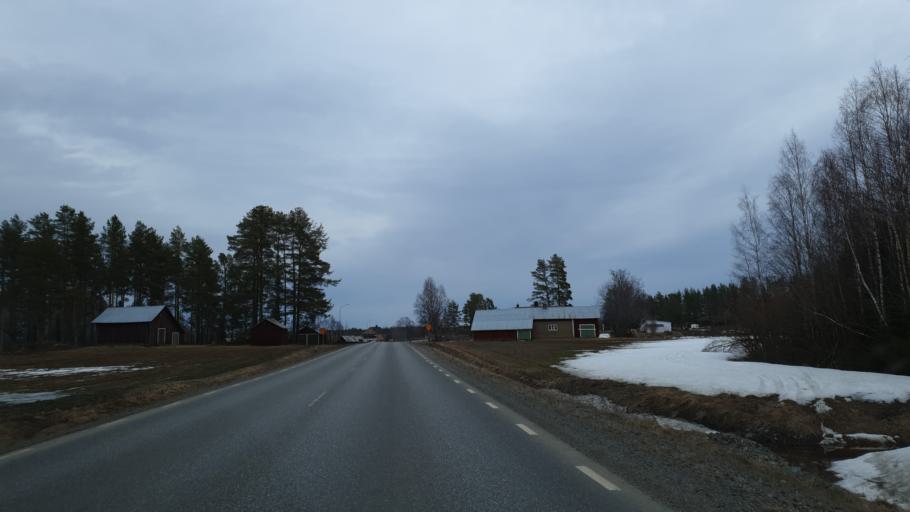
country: SE
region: Vaesterbotten
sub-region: Robertsfors Kommun
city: Robertsfors
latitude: 64.2289
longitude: 20.9443
